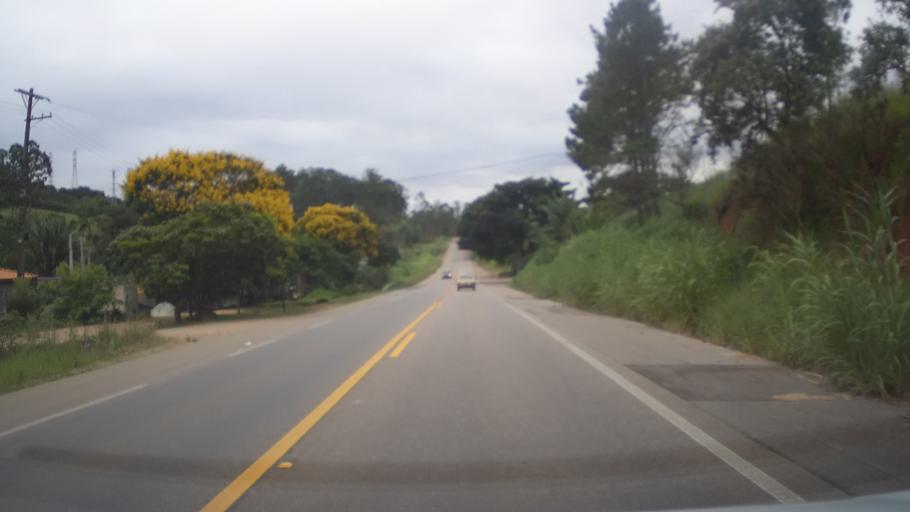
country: BR
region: Sao Paulo
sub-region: Louveira
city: Louveira
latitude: -23.1138
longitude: -46.9413
